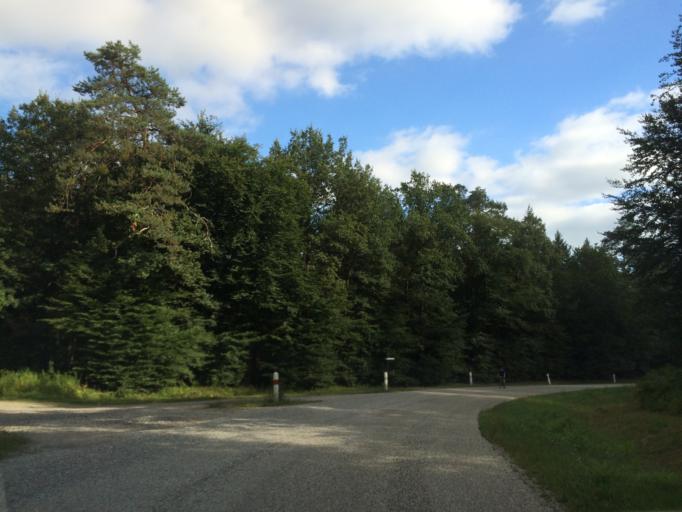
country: FR
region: Alsace
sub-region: Departement du Bas-Rhin
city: Soufflenheim
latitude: 48.8472
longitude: 7.9577
